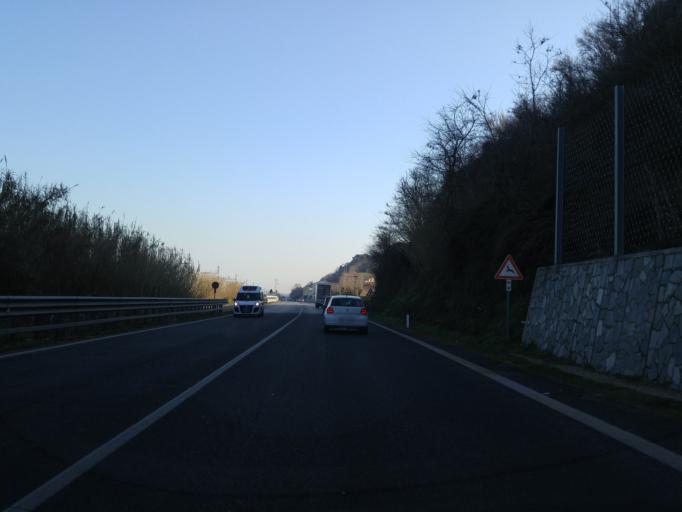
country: IT
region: The Marches
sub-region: Provincia di Pesaro e Urbino
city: Fenile
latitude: 43.8821
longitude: 12.9600
